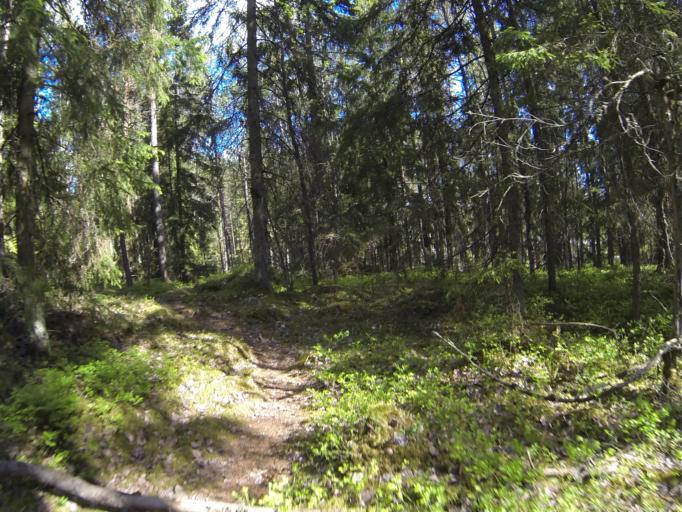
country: FI
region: Varsinais-Suomi
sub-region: Salo
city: Salo
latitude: 60.3837
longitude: 23.1787
